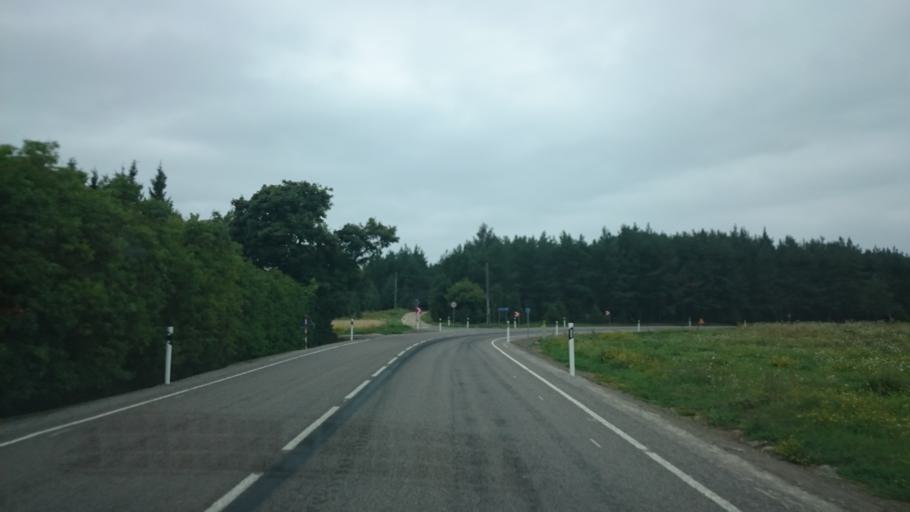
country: EE
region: Saare
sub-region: Orissaare vald
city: Orissaare
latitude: 58.5873
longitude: 22.7057
